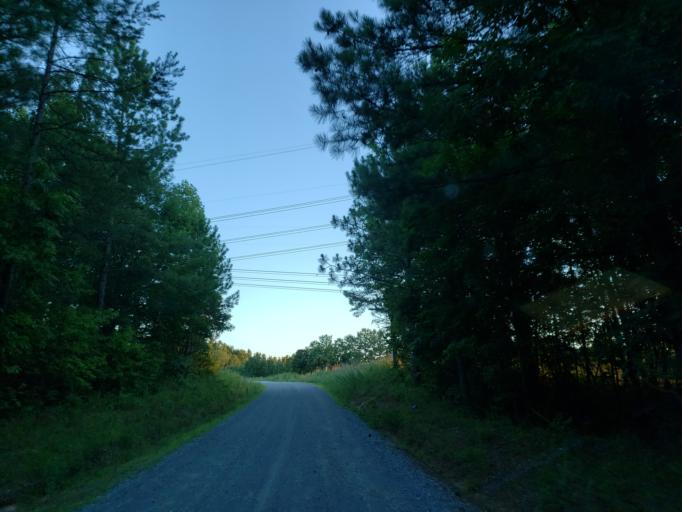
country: US
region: Georgia
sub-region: Bartow County
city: Euharlee
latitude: 34.0627
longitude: -84.8545
